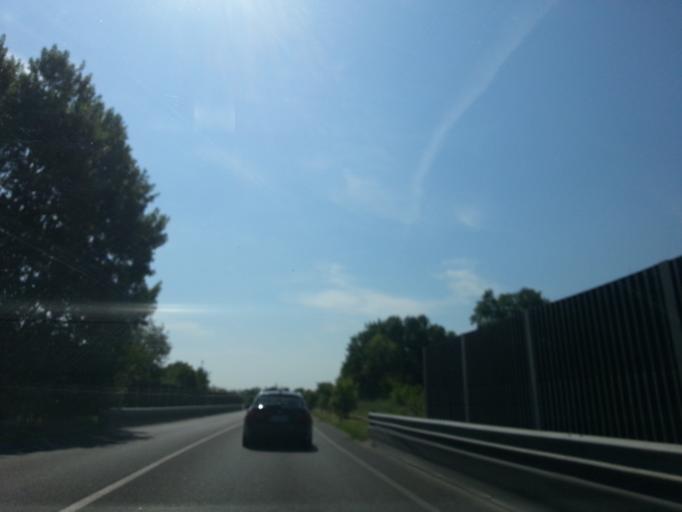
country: IT
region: Emilia-Romagna
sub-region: Provincia di Reggio Emilia
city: Albinea
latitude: 44.6661
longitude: 10.6051
